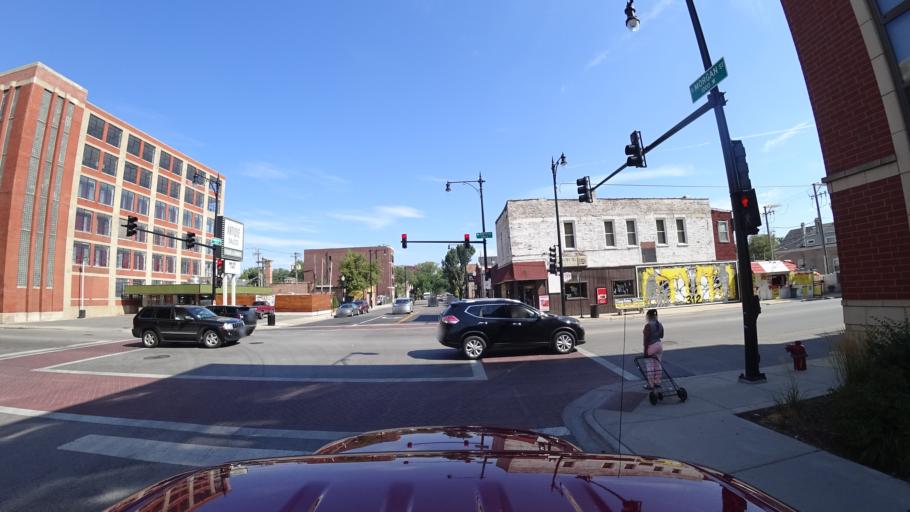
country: US
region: Illinois
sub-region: Cook County
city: Chicago
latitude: 41.8306
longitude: -87.6509
